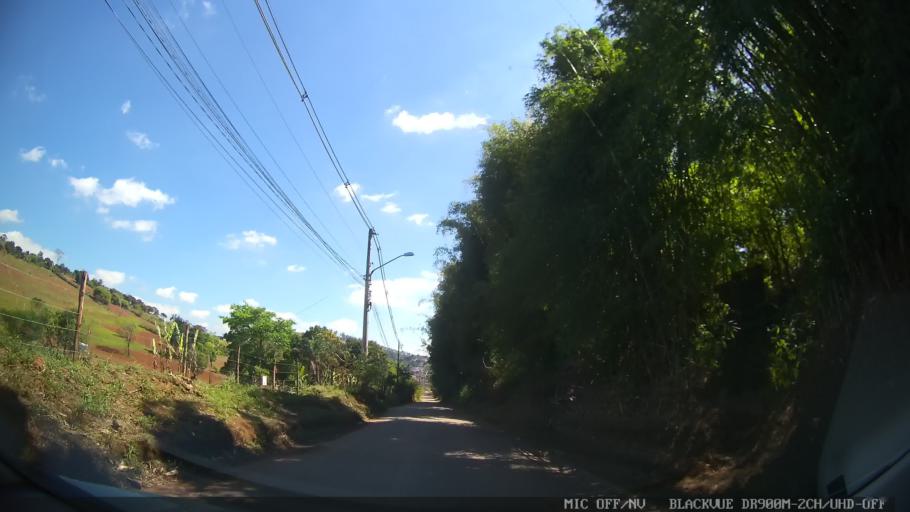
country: BR
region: Sao Paulo
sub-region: Cajamar
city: Cajamar
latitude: -23.4142
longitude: -46.8155
